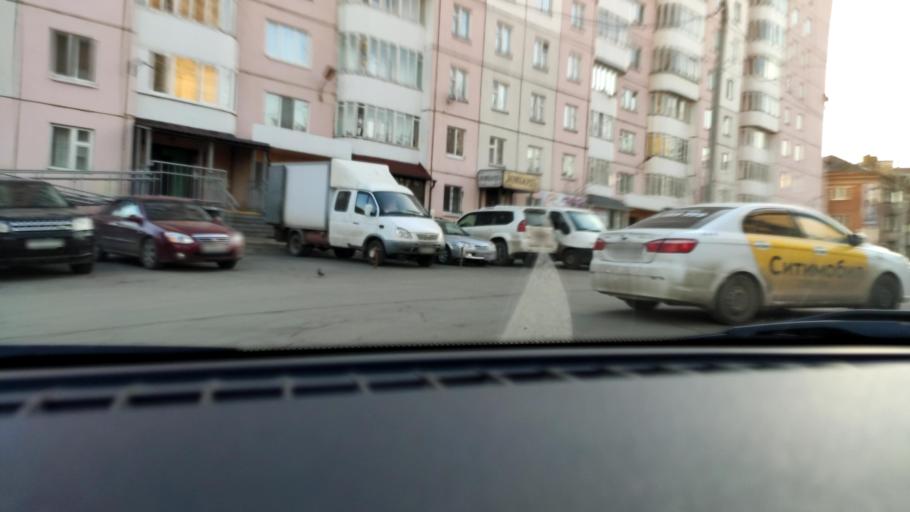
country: RU
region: Perm
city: Perm
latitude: 57.9769
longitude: 56.2103
